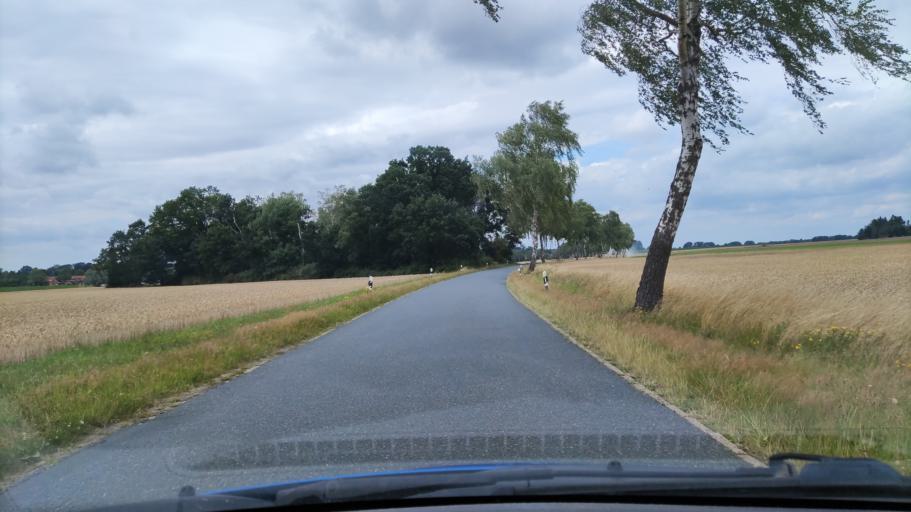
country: DE
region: Lower Saxony
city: Altenmedingen
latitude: 53.1404
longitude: 10.6294
